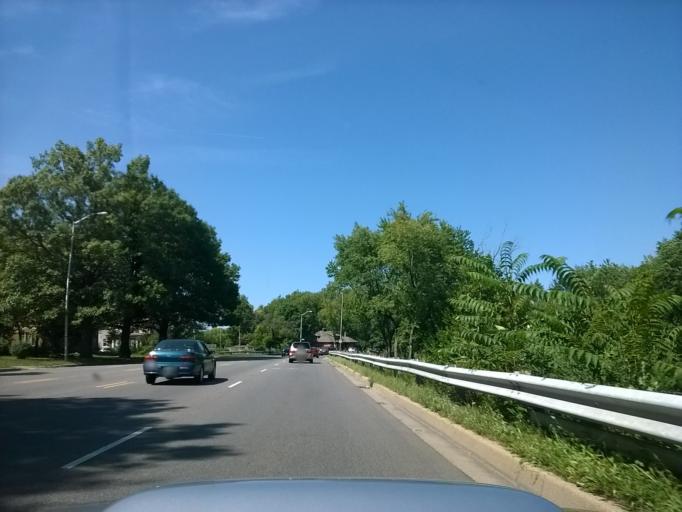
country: US
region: Indiana
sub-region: Marion County
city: Indianapolis
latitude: 39.8127
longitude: -86.1437
